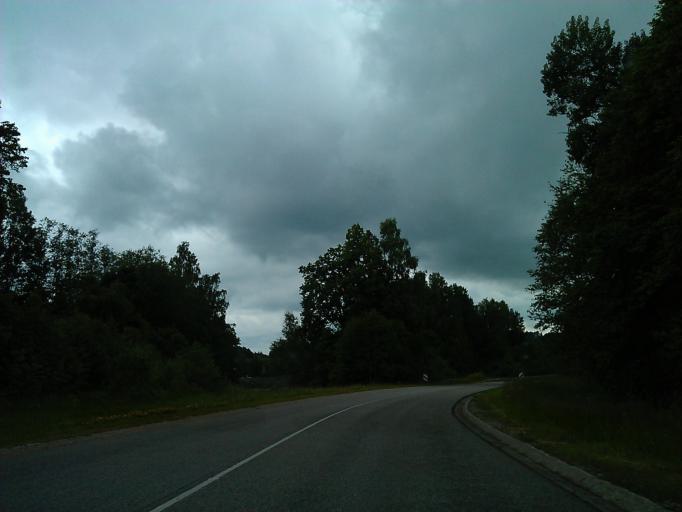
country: LV
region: Kuldigas Rajons
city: Kuldiga
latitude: 56.8649
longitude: 21.8528
